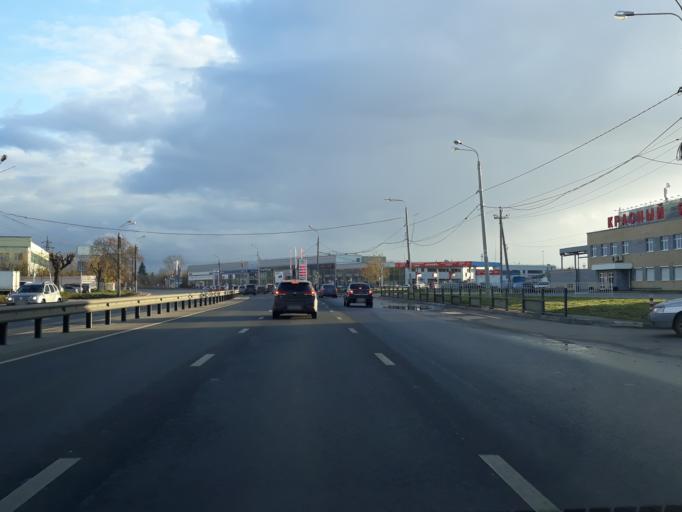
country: RU
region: Nizjnij Novgorod
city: Nizhniy Novgorod
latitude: 56.3118
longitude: 43.8993
